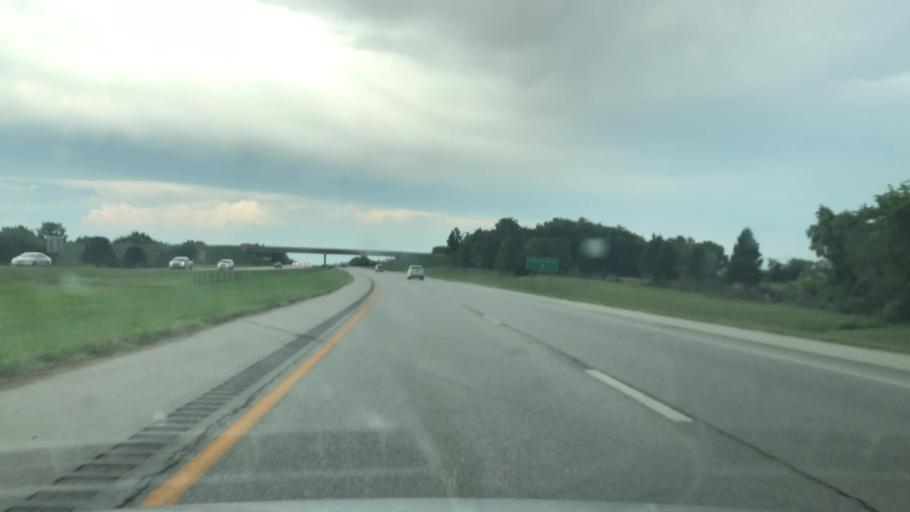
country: US
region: Oklahoma
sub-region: Tulsa County
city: Turley
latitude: 36.2612
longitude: -95.9233
